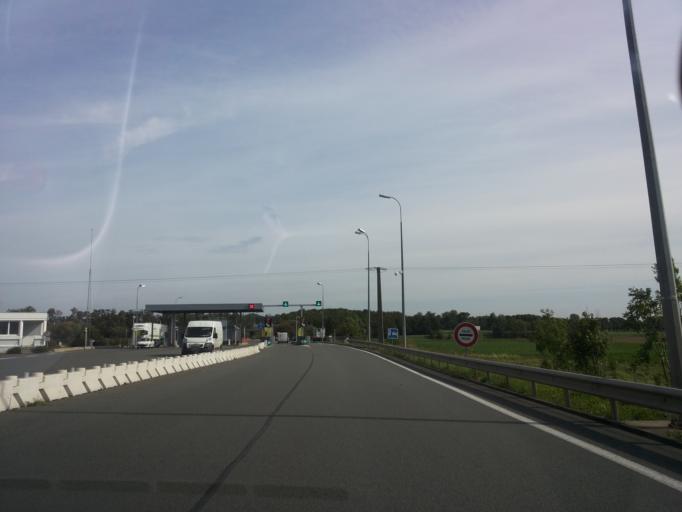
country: FR
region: Nord-Pas-de-Calais
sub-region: Departement du Pas-de-Calais
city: Thelus
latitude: 50.3446
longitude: 2.7866
